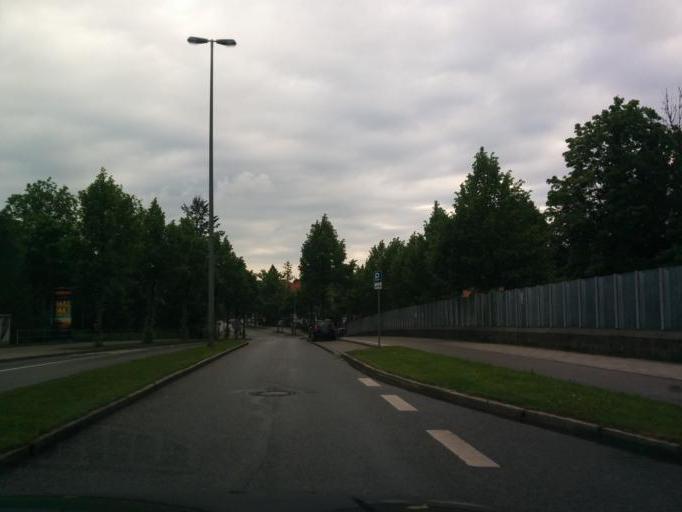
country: DE
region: Bavaria
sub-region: Upper Bavaria
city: Pullach im Isartal
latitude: 48.0789
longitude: 11.5273
